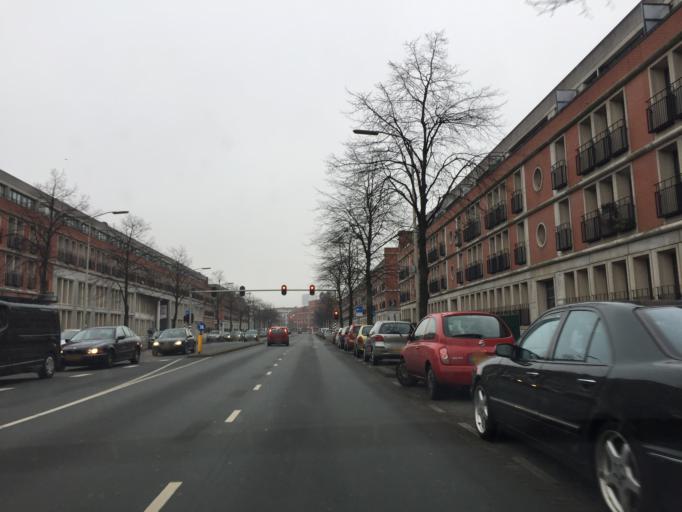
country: NL
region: South Holland
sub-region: Gemeente Den Haag
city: The Hague
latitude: 52.0684
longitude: 4.3024
